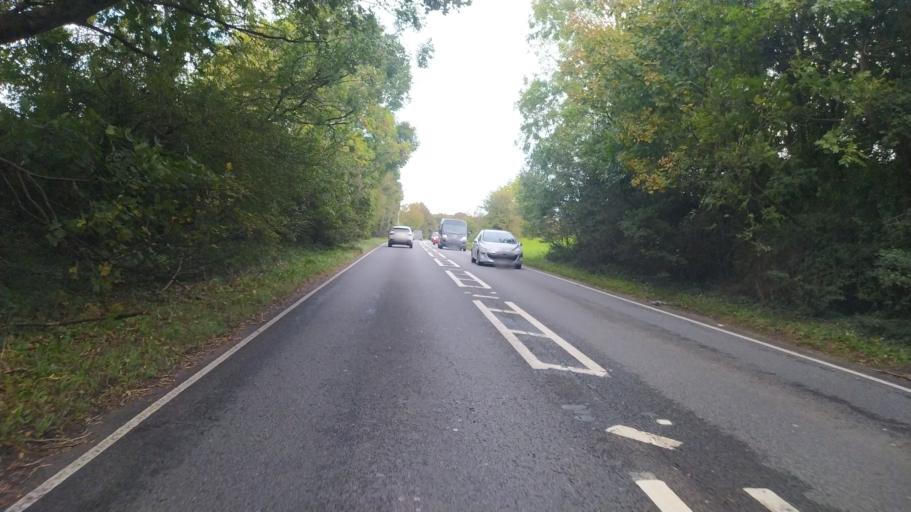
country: GB
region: England
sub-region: Dorset
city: Dorchester
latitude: 50.7276
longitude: -2.4069
